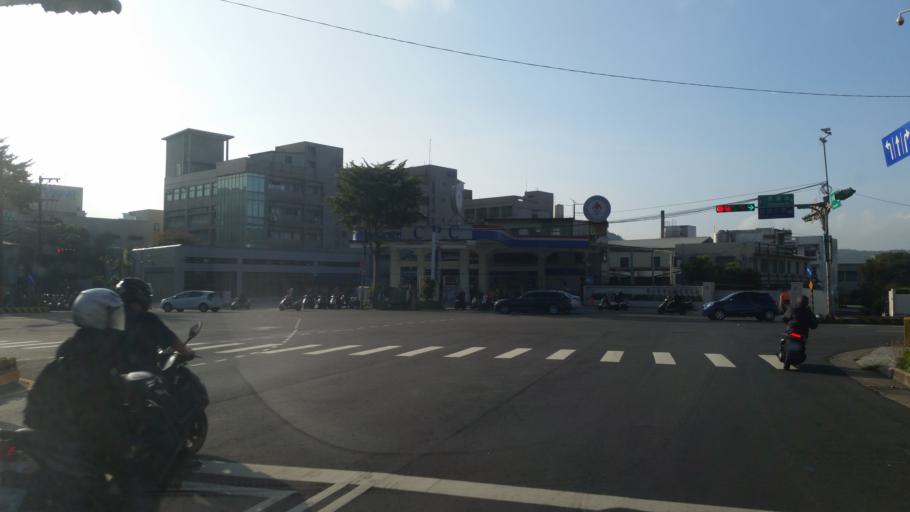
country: TW
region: Taiwan
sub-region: Taoyuan
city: Taoyuan
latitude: 25.0020
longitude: 121.3438
